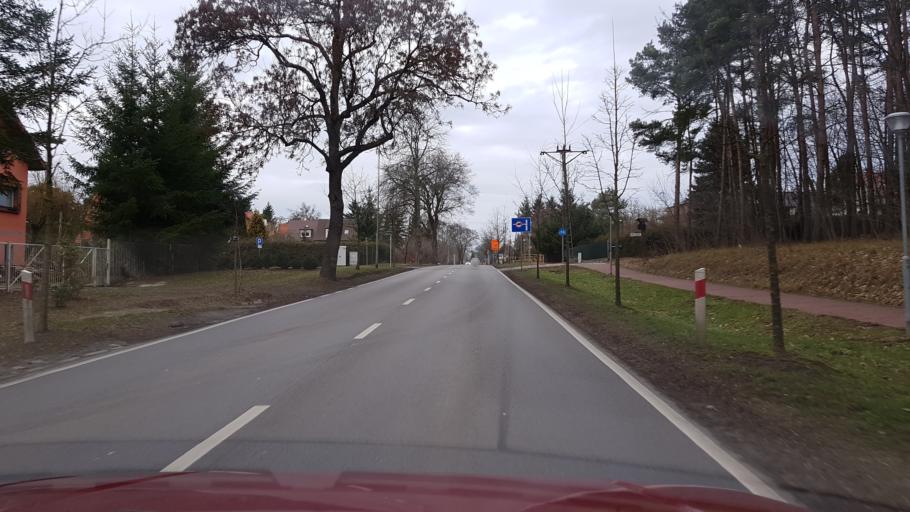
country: PL
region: West Pomeranian Voivodeship
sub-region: Szczecin
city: Szczecin
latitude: 53.4908
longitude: 14.4812
